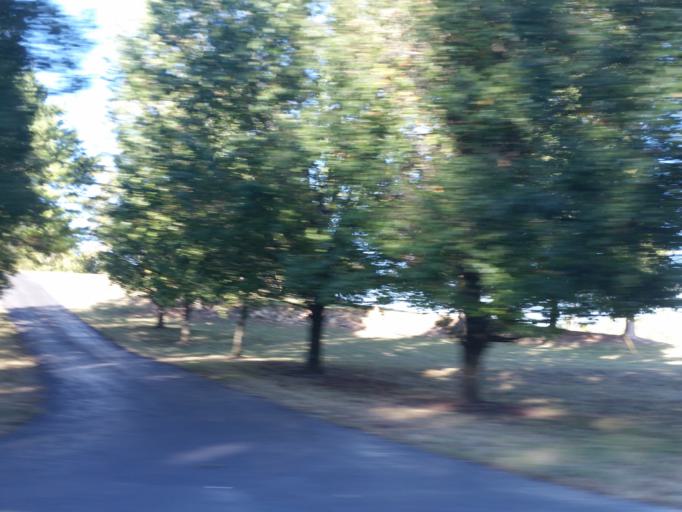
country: US
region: Tennessee
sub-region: Grainger County
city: Rutledge
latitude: 36.2390
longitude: -83.6167
